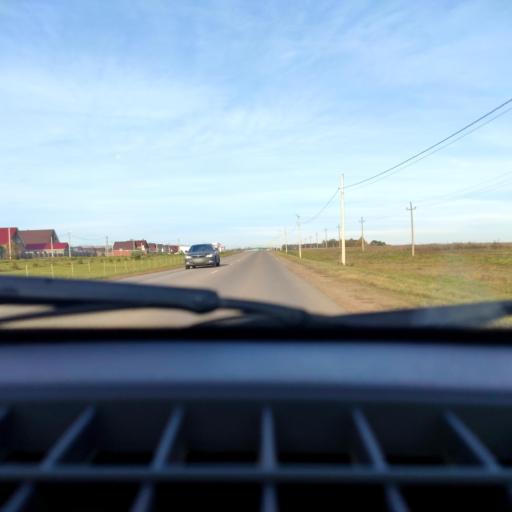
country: RU
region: Bashkortostan
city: Avdon
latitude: 54.6579
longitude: 55.7458
